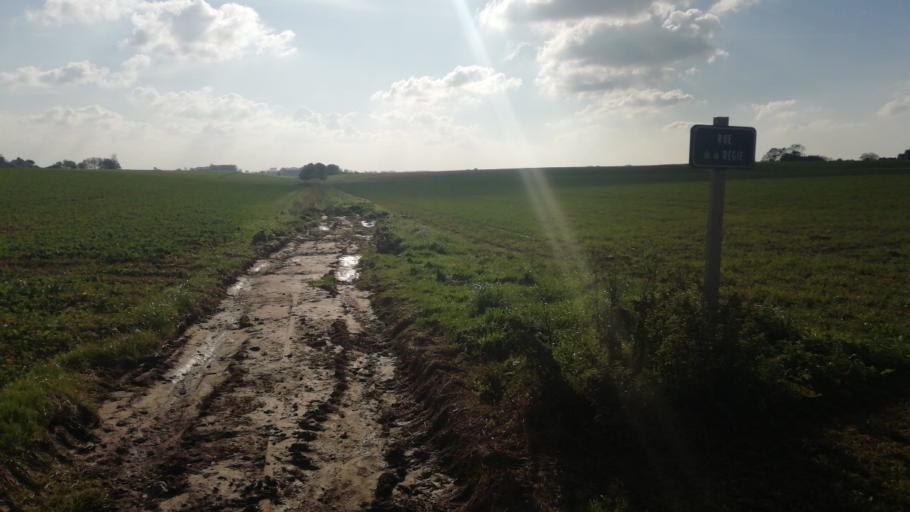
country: FR
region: Haute-Normandie
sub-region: Departement de la Seine-Maritime
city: Turretot
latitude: 49.6288
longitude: 0.2492
